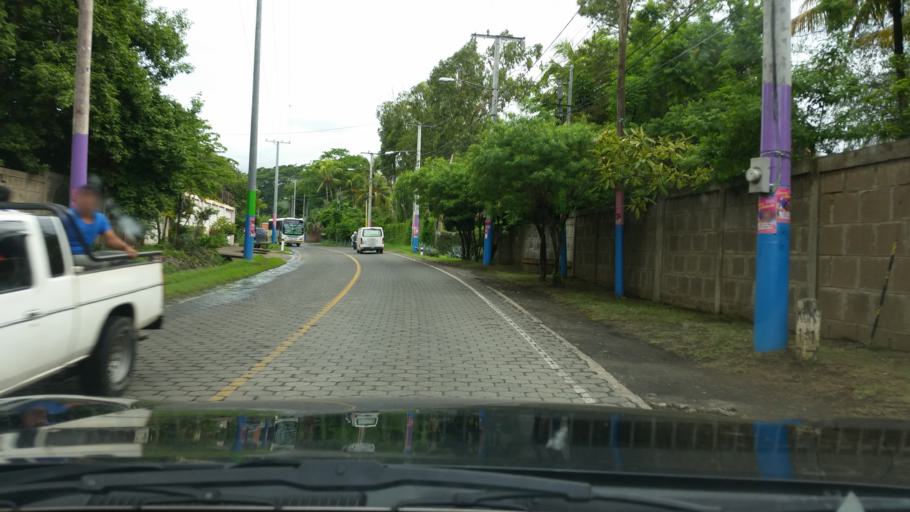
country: NI
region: Masaya
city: Ticuantepe
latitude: 12.0334
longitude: -86.2066
